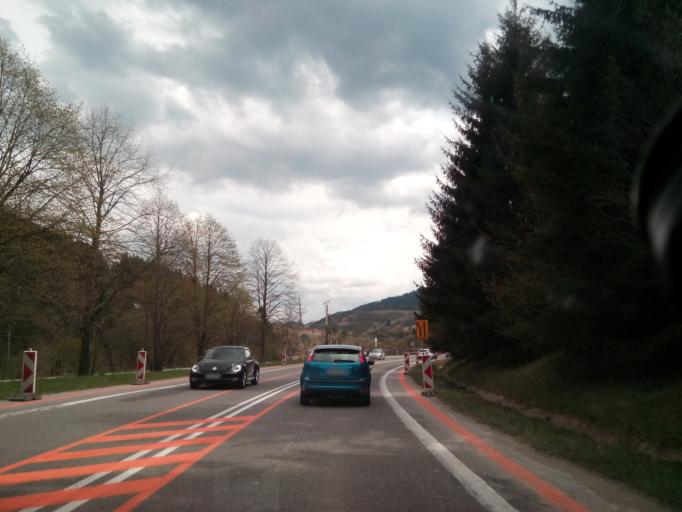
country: SK
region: Zilinsky
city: Ruzomberok
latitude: 49.1183
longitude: 19.2261
